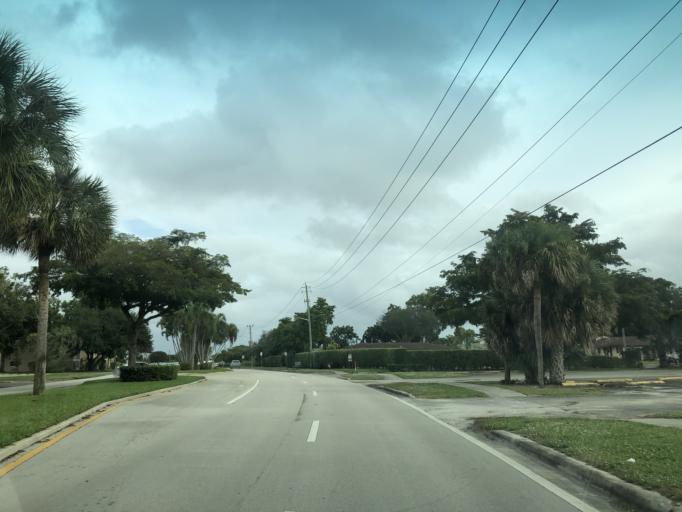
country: US
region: Florida
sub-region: Broward County
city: North Lauderdale
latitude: 26.2403
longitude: -80.2298
